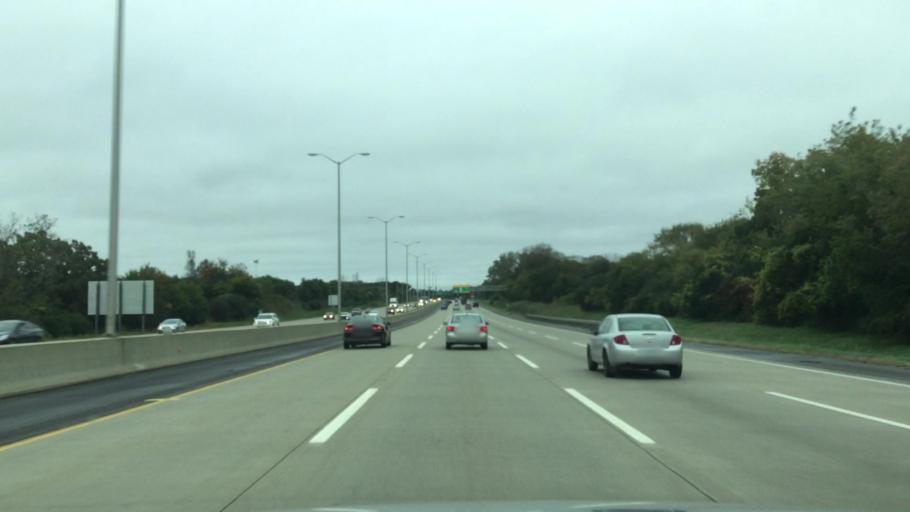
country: US
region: Illinois
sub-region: Lake County
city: Wadsworth
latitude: 42.4458
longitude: -87.9581
